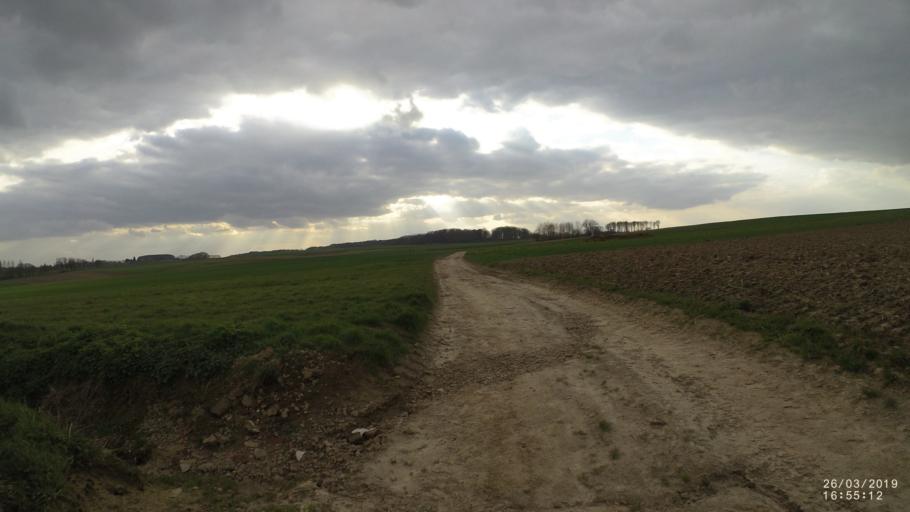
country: BE
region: Flanders
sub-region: Provincie Vlaams-Brabant
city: Bertem
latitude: 50.8409
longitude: 4.6234
